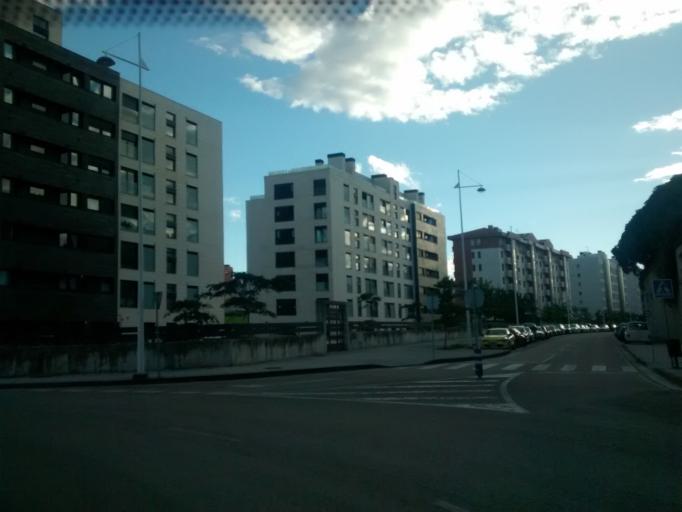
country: ES
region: Cantabria
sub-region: Provincia de Cantabria
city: Santander
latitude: 43.4741
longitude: -3.8100
